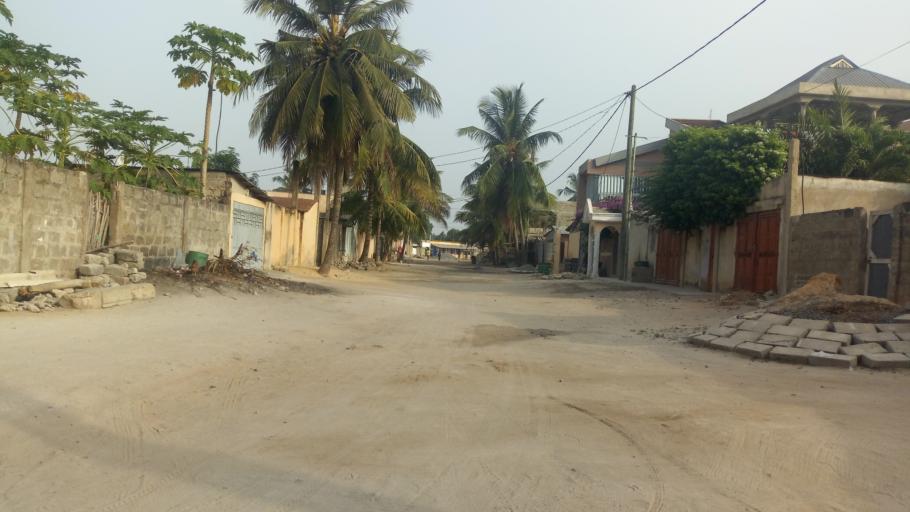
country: TG
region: Maritime
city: Lome
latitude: 6.1765
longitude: 1.1710
